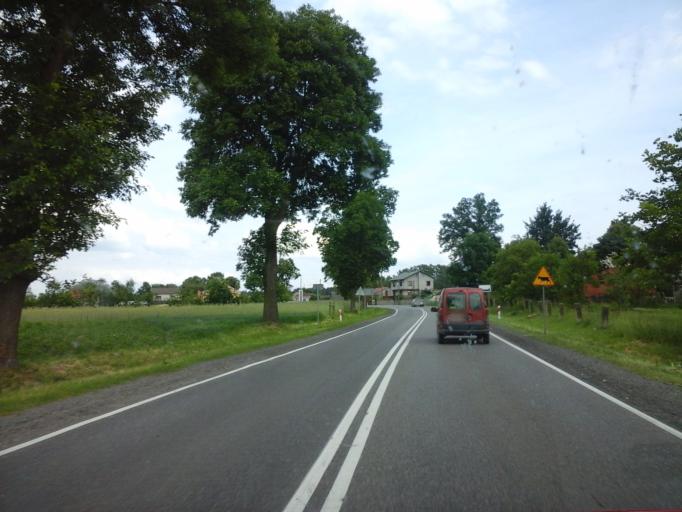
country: PL
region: Lodz Voivodeship
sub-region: Powiat opoczynski
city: Paradyz
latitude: 51.3153
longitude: 20.0672
